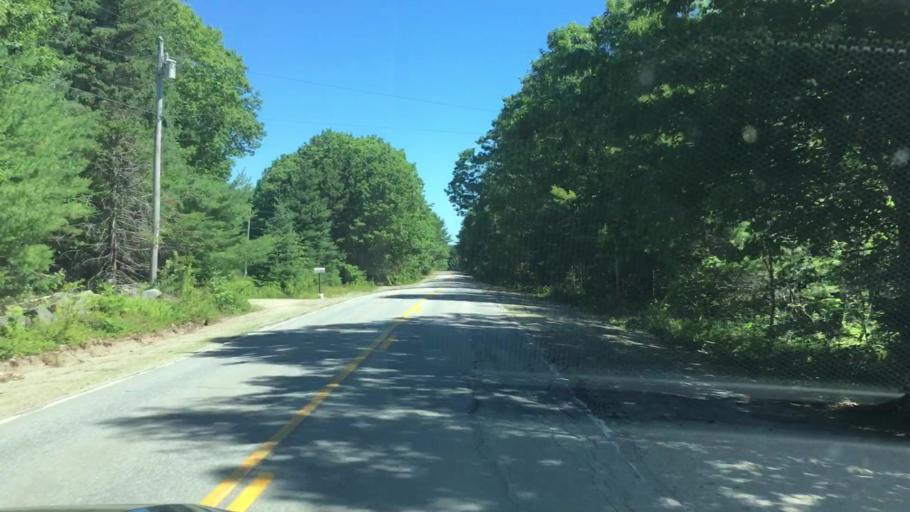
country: US
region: Maine
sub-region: Hancock County
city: Penobscot
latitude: 44.4412
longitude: -68.7064
